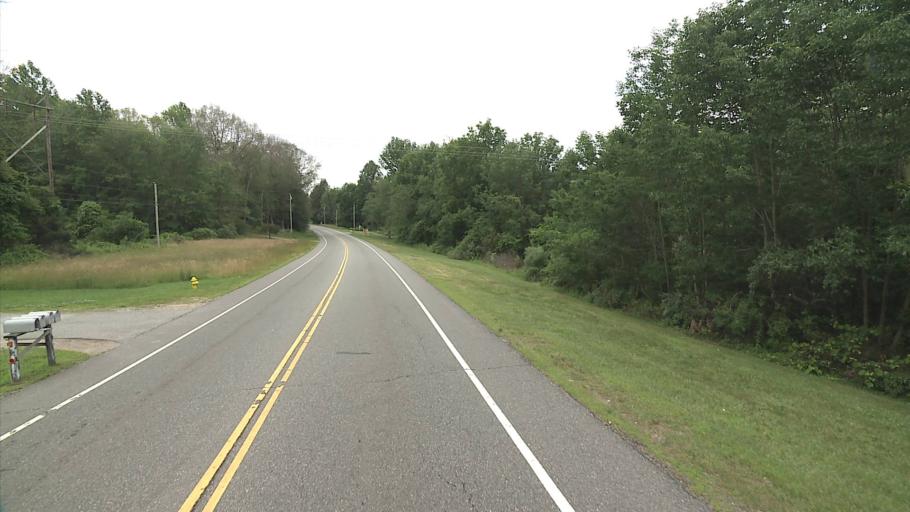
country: US
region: Connecticut
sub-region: New London County
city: Ledyard Center
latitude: 41.4039
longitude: -72.0246
